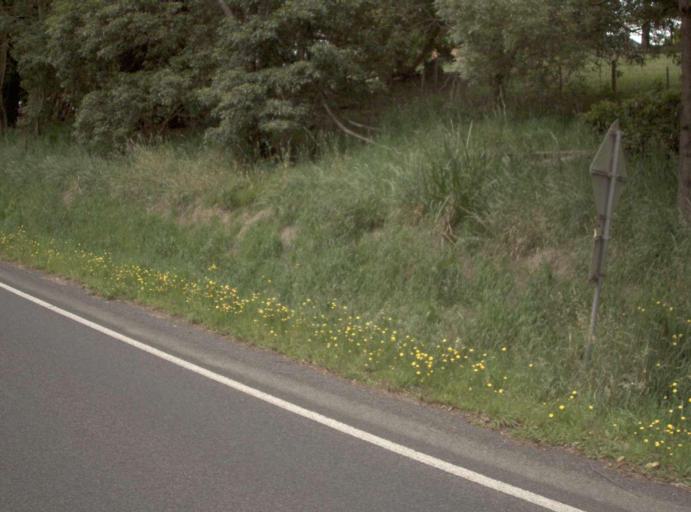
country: AU
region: Victoria
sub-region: Latrobe
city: Moe
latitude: -38.6181
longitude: 146.1458
